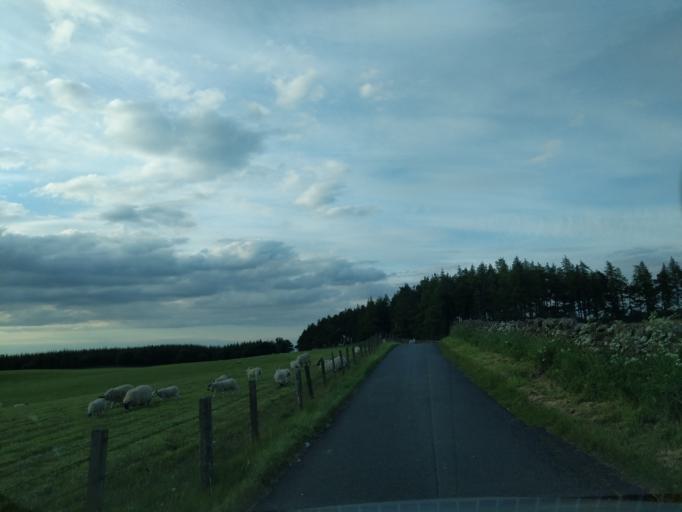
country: GB
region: Scotland
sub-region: Midlothian
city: Gorebridge
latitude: 55.7829
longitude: -3.0974
